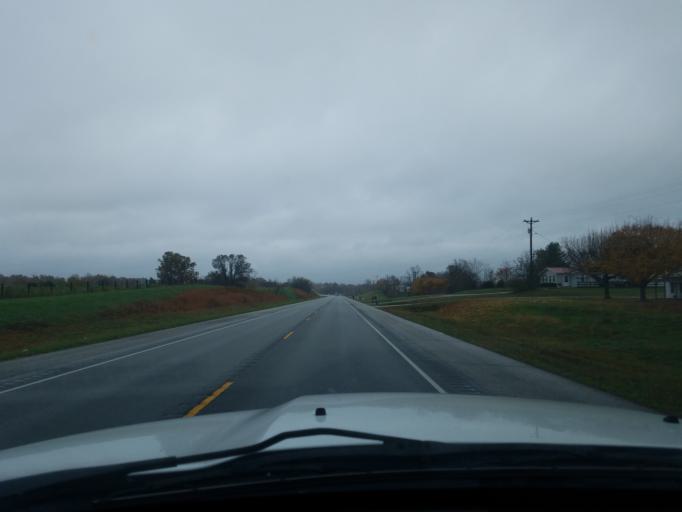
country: US
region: Kentucky
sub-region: Larue County
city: Hodgenville
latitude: 37.5288
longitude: -85.6812
